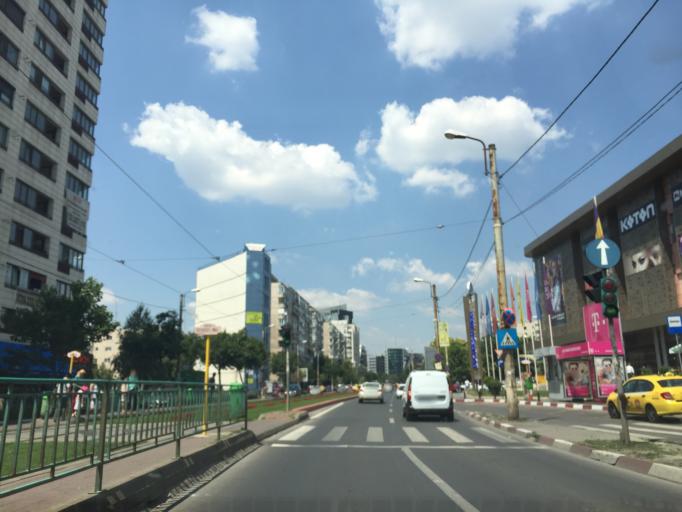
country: RO
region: Bucuresti
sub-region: Municipiul Bucuresti
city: Bucharest
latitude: 44.4198
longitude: 26.1261
